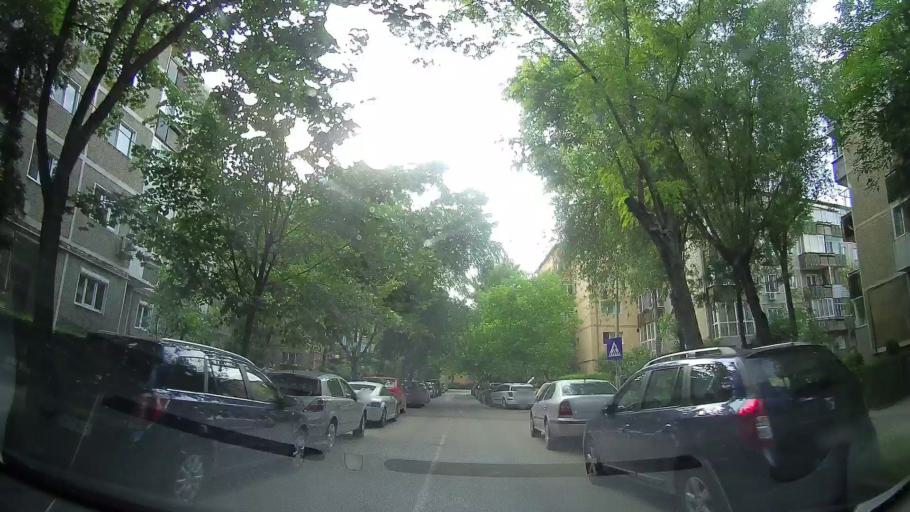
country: RO
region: Timis
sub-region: Comuna Dumbravita
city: Dumbravita
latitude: 45.7773
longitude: 21.2389
